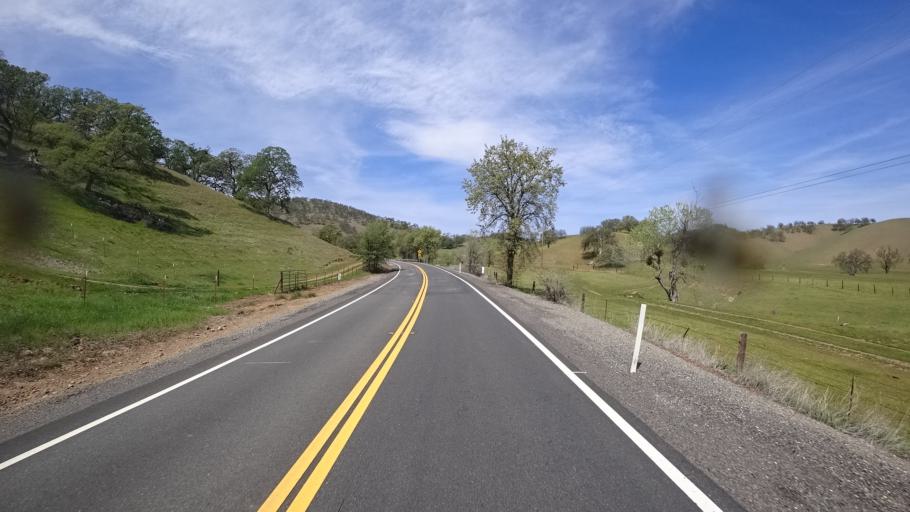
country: US
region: California
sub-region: Glenn County
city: Willows
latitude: 39.5944
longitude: -122.4621
